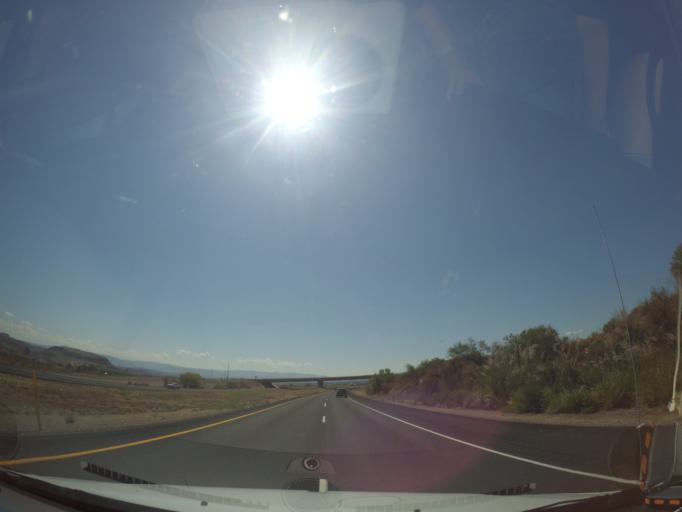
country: US
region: Utah
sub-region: Washington County
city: Washington
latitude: 37.1489
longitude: -113.4852
